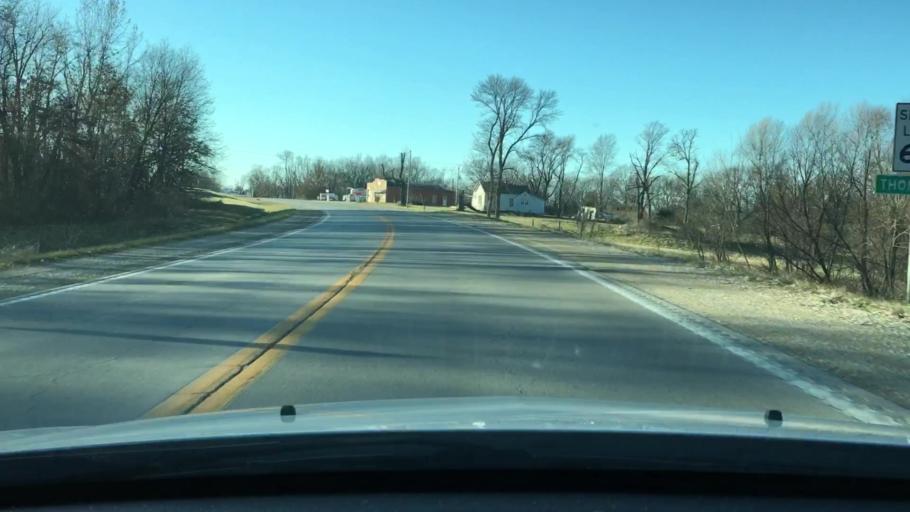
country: US
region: Missouri
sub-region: Audrain County
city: Mexico
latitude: 39.1898
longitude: -91.9800
